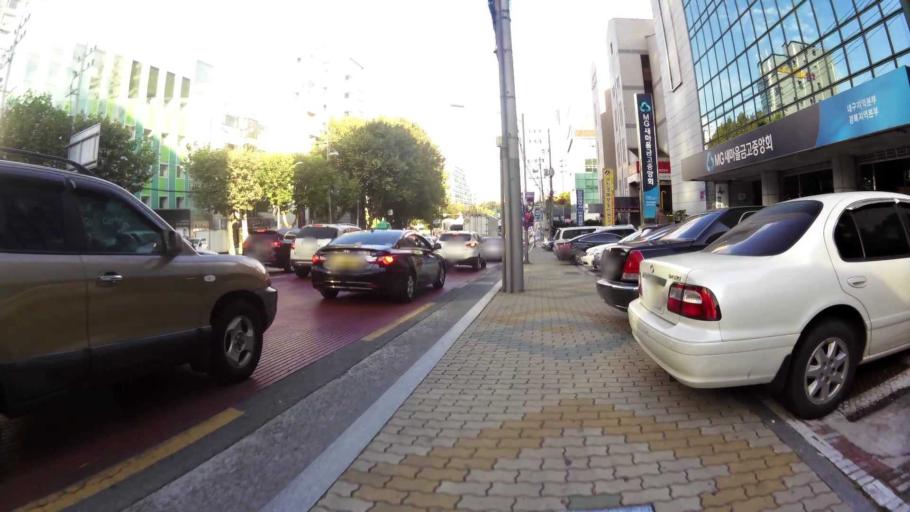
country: KR
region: Daegu
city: Daegu
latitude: 35.8671
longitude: 128.6252
